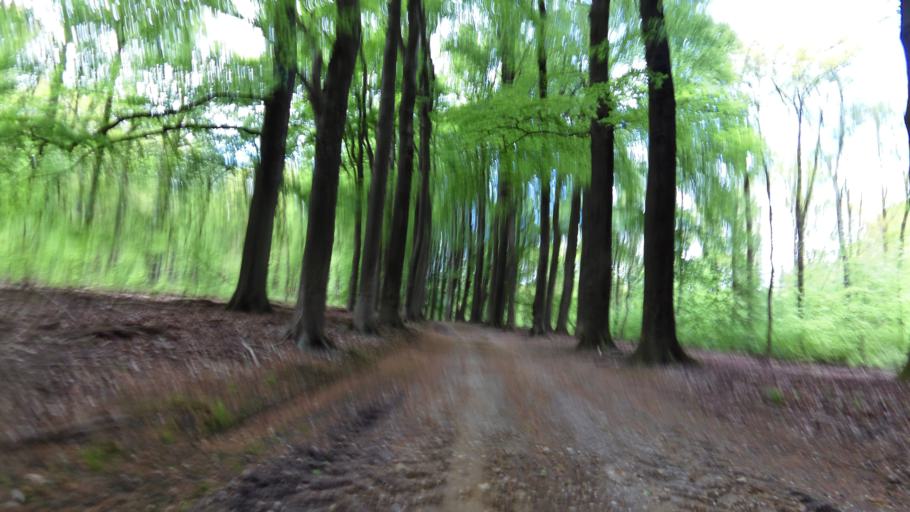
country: NL
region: Gelderland
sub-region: Gemeente Rheden
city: De Steeg
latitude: 52.0428
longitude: 6.0451
